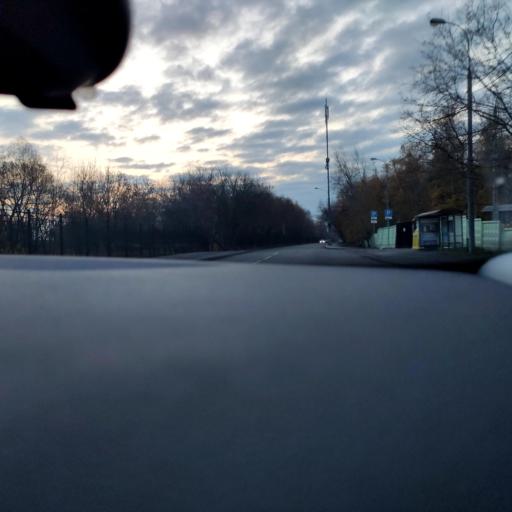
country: RU
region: Moscow
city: Kuz'minki
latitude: 55.6818
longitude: 37.7865
